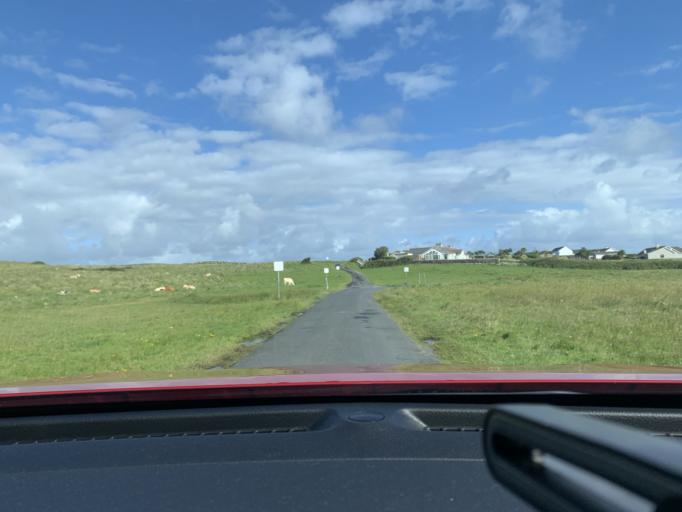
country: IE
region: Connaught
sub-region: Sligo
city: Strandhill
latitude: 54.4008
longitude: -8.5648
